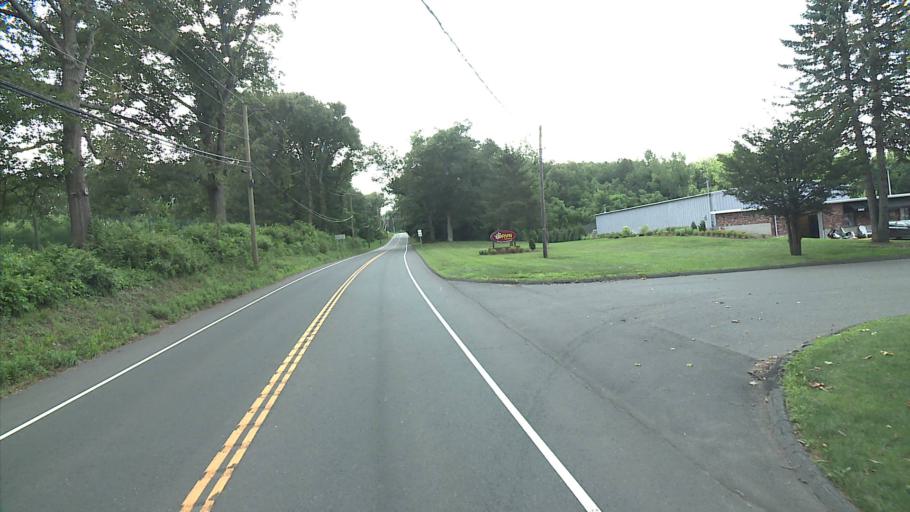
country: US
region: Connecticut
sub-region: Middlesex County
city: Portland
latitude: 41.5784
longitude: -72.6075
